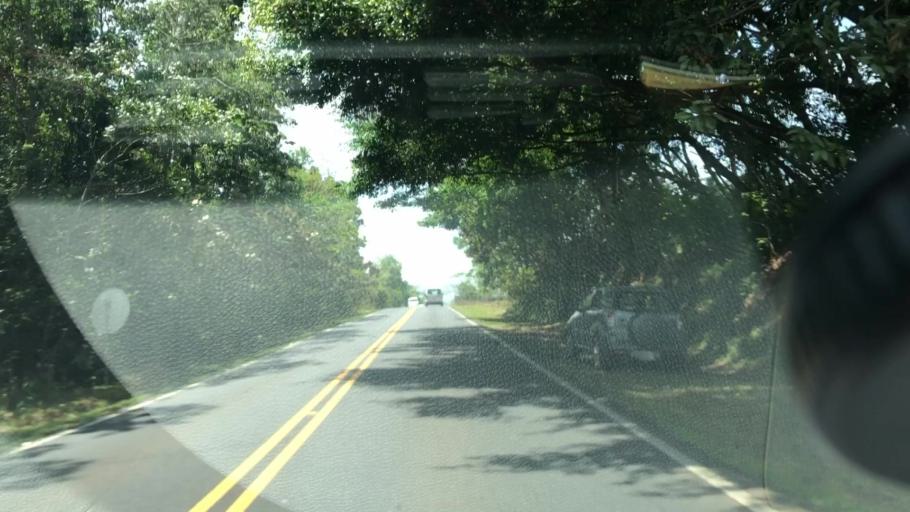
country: CR
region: Alajuela
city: Pital
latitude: 10.4580
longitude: -84.3950
